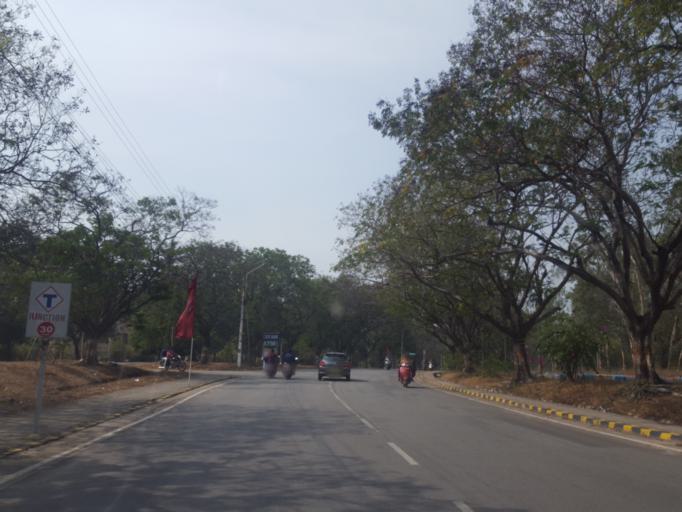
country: IN
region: Telangana
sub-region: Medak
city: Serilingampalle
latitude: 17.4924
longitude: 78.3096
